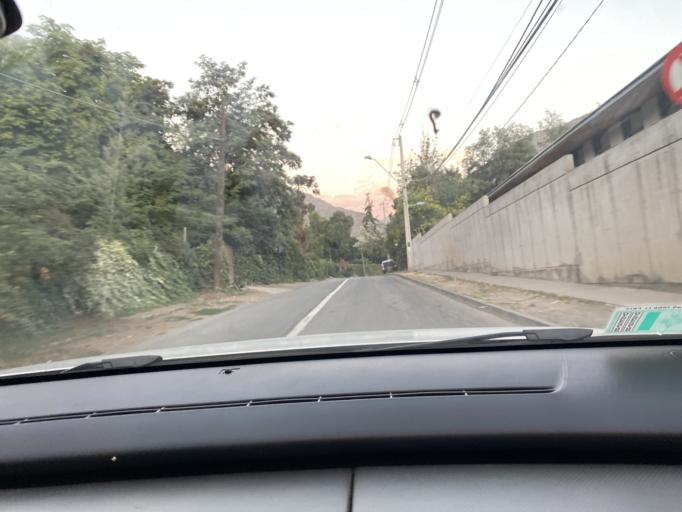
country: CL
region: Santiago Metropolitan
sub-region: Provincia de Santiago
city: Villa Presidente Frei, Nunoa, Santiago, Chile
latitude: -33.3607
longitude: -70.4840
